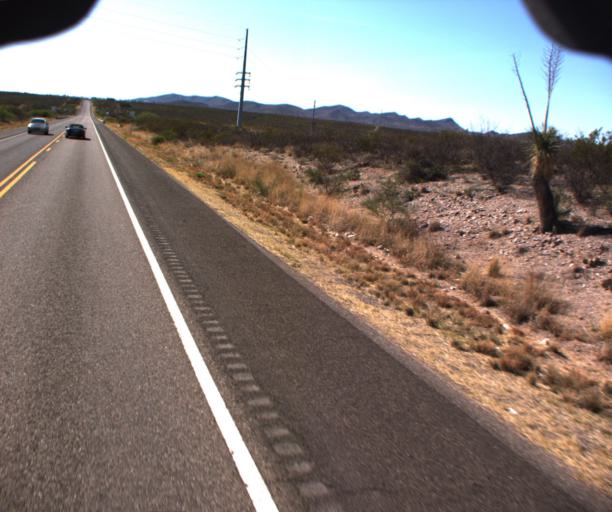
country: US
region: Arizona
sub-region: Cochise County
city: Tombstone
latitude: 31.7458
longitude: -110.0942
